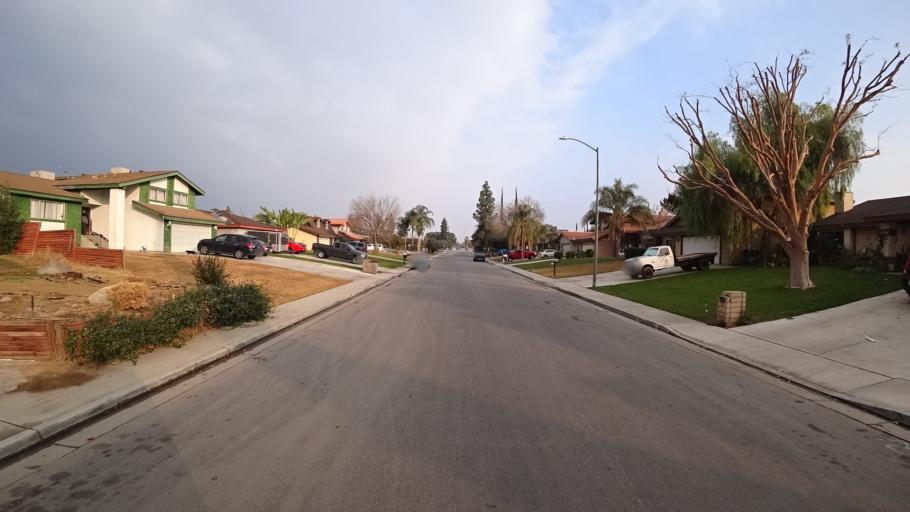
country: US
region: California
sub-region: Kern County
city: Greenfield
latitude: 35.3160
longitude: -119.0439
